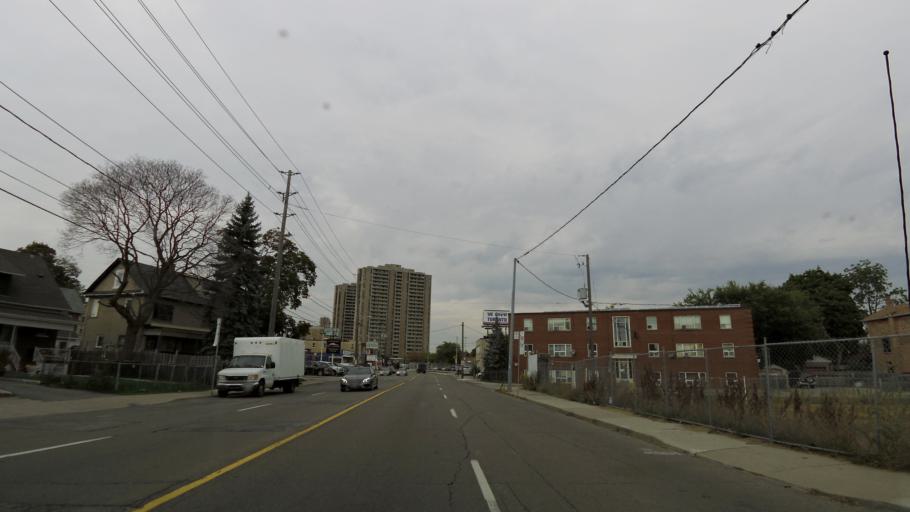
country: CA
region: Ontario
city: Etobicoke
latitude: 43.6970
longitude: -79.5090
